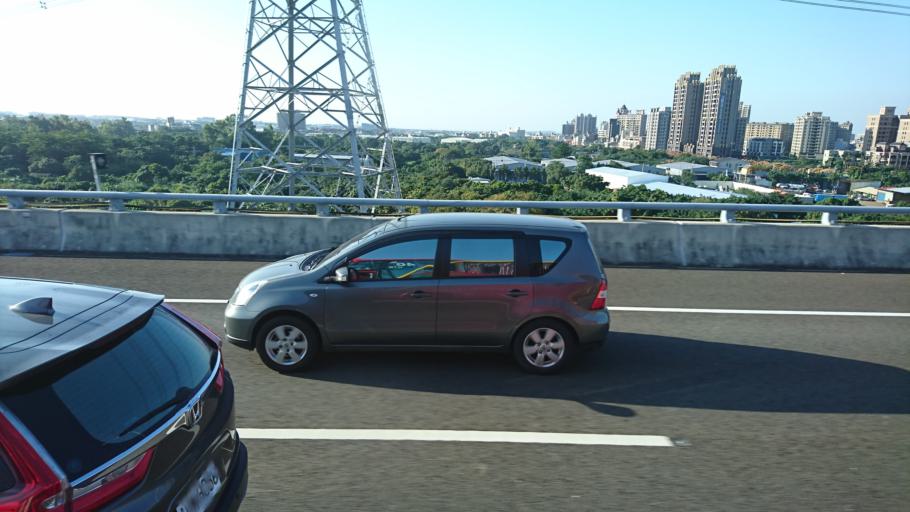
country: TW
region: Taiwan
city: Taoyuan City
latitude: 25.0100
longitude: 121.2617
